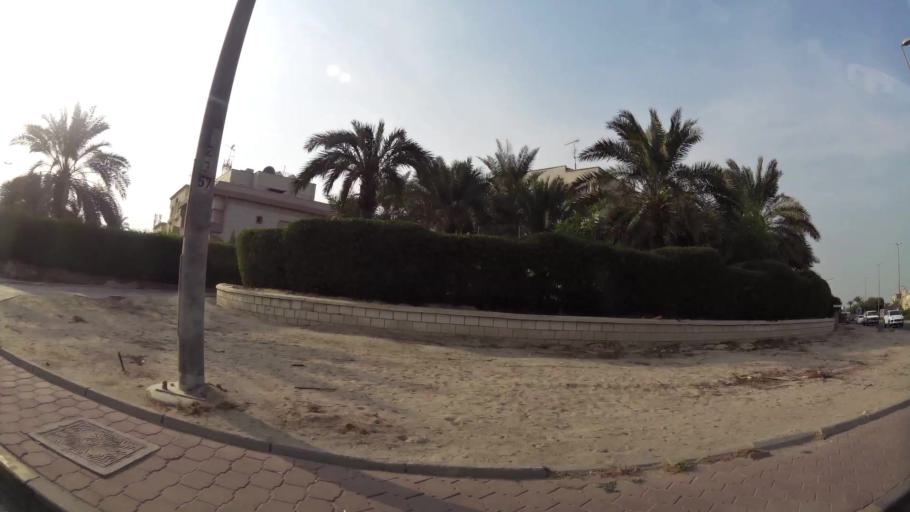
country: KW
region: Mubarak al Kabir
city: Sabah as Salim
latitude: 29.2375
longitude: 48.0617
